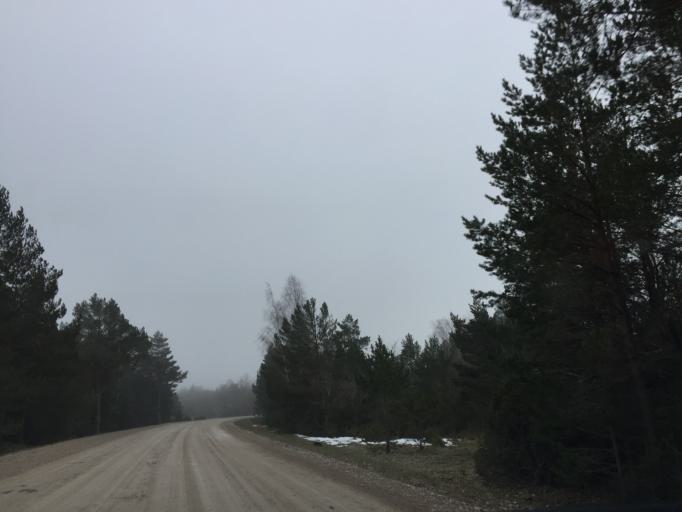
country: EE
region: Saare
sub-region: Kuressaare linn
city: Kuressaare
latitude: 58.4773
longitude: 22.0018
